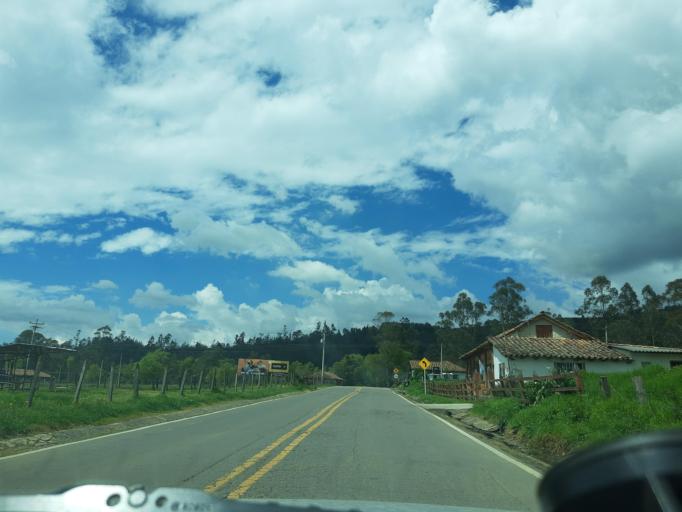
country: CO
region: Boyaca
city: Chiquinquira
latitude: 5.6079
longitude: -73.7276
